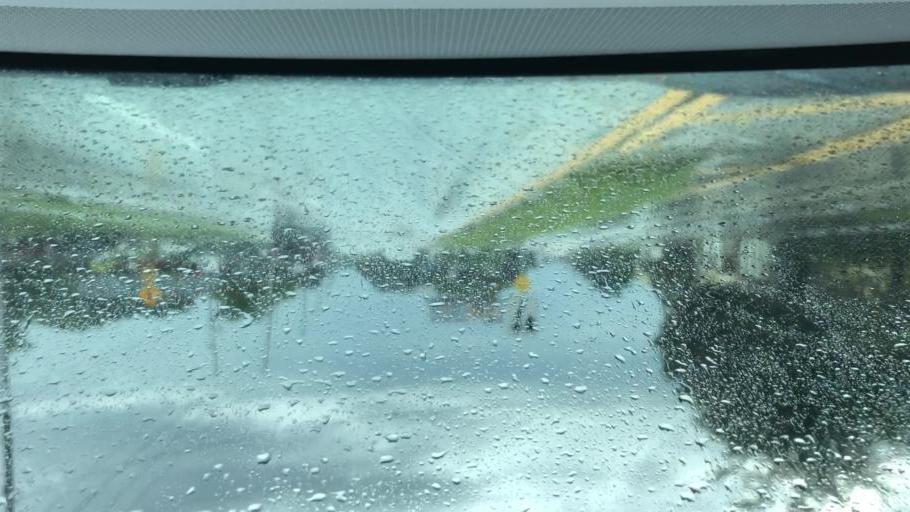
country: US
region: Florida
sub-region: Orange County
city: Pine Castle
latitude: 28.4675
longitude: -81.3677
